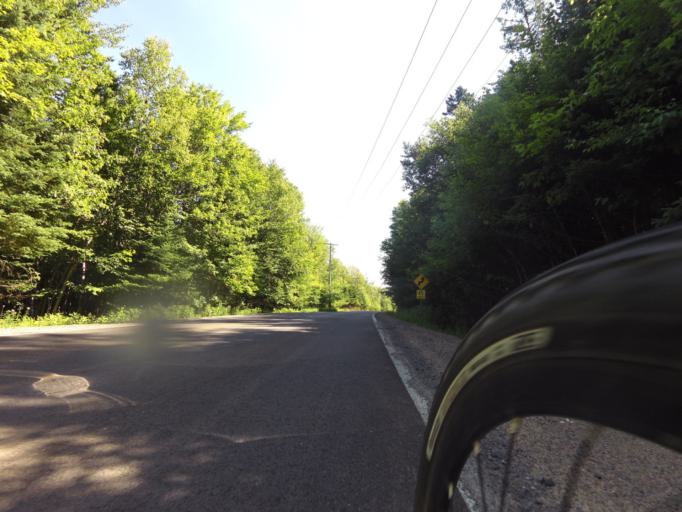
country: CA
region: Quebec
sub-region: Laurentides
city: Brownsburg-Chatham
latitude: 45.8425
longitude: -74.5349
